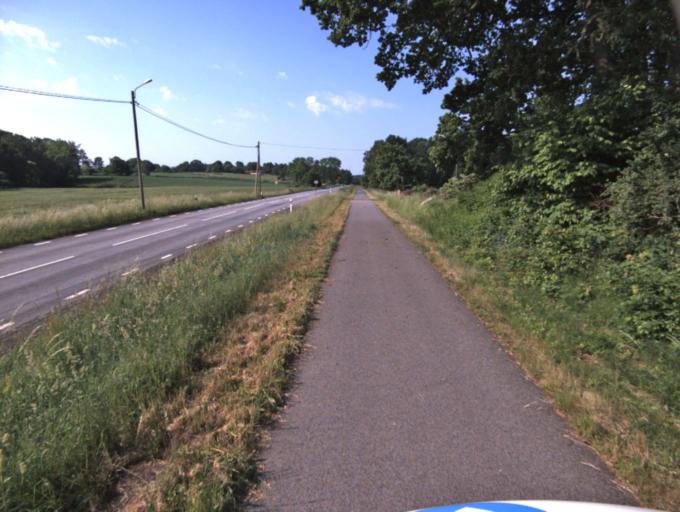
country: SE
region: Skane
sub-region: Kristianstads Kommun
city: Tollarp
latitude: 56.1662
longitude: 14.2804
